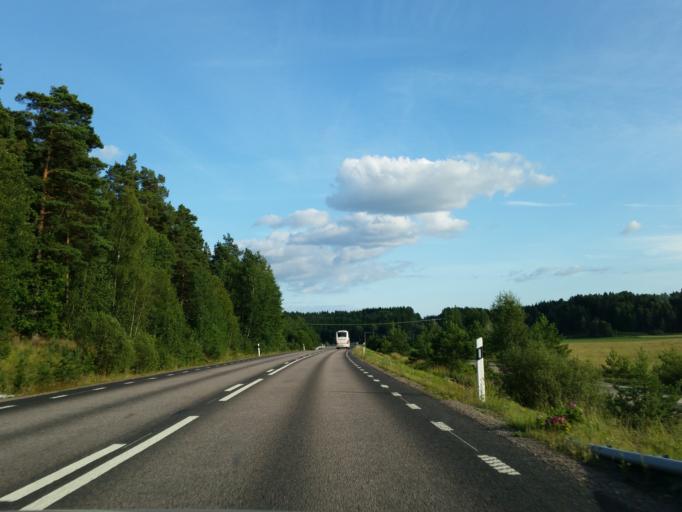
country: SE
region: Soedermanland
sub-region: Gnesta Kommun
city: Gnesta
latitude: 59.0426
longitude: 17.2926
